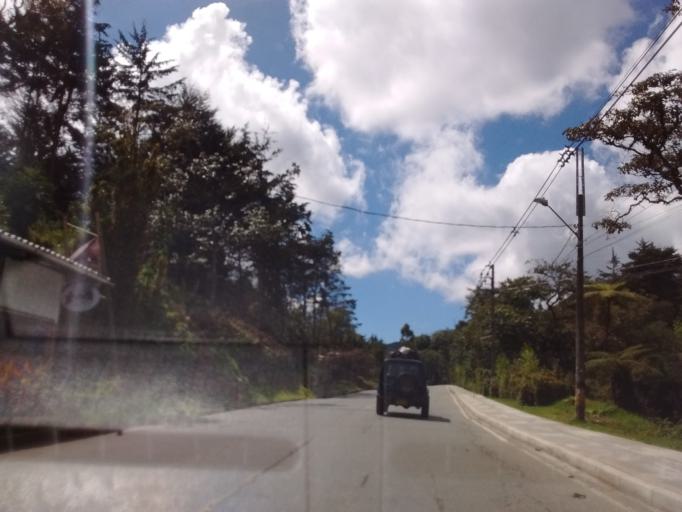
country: CO
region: Antioquia
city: Medellin
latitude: 6.2117
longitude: -75.5013
